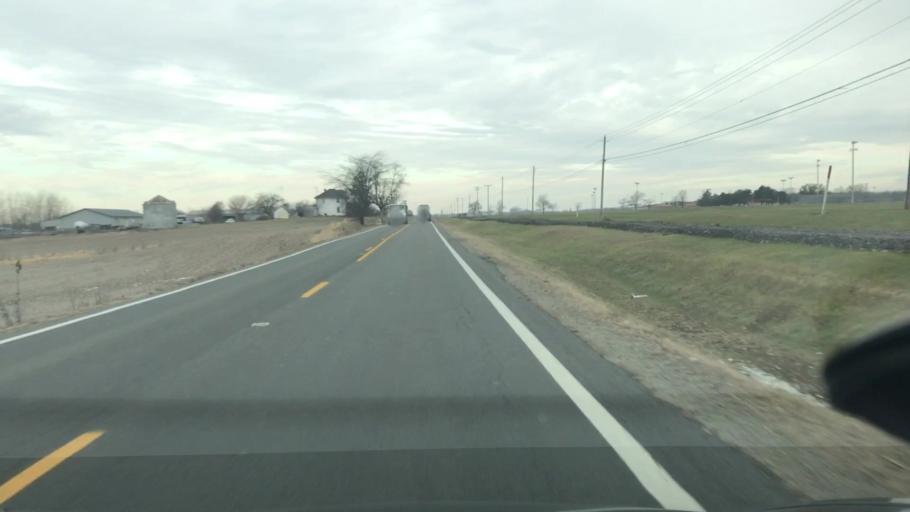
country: US
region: Ohio
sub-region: Madison County
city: London
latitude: 39.9051
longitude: -83.4697
